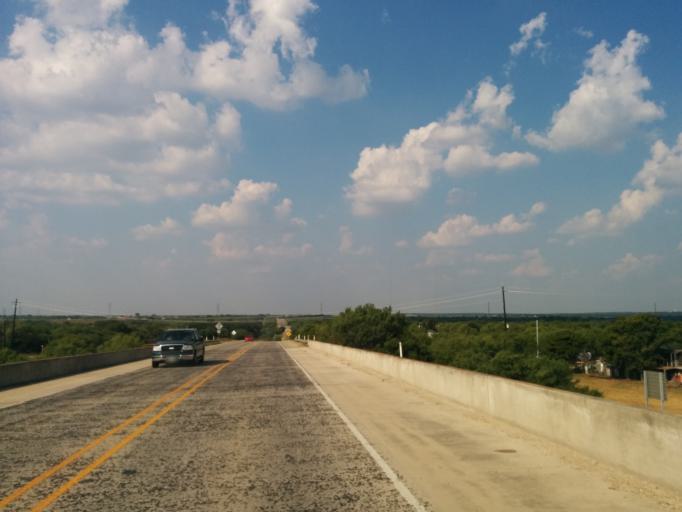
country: US
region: Texas
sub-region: Bexar County
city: Elmendorf
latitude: 29.2672
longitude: -98.3065
